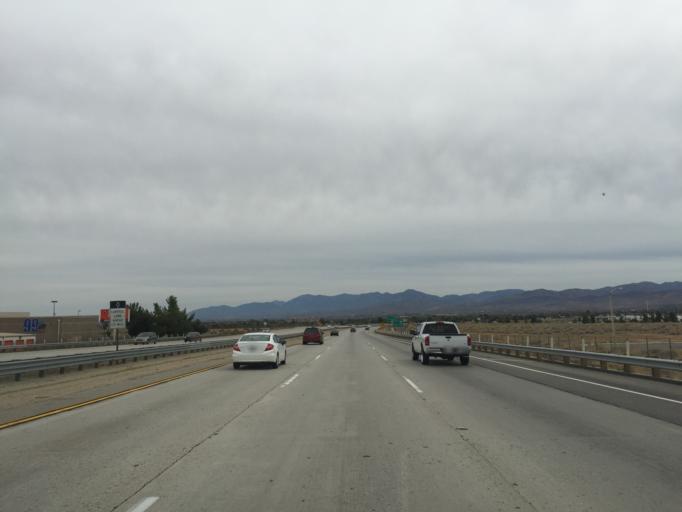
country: US
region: California
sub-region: Los Angeles County
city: Desert View Highlands
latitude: 34.5991
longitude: -118.1393
